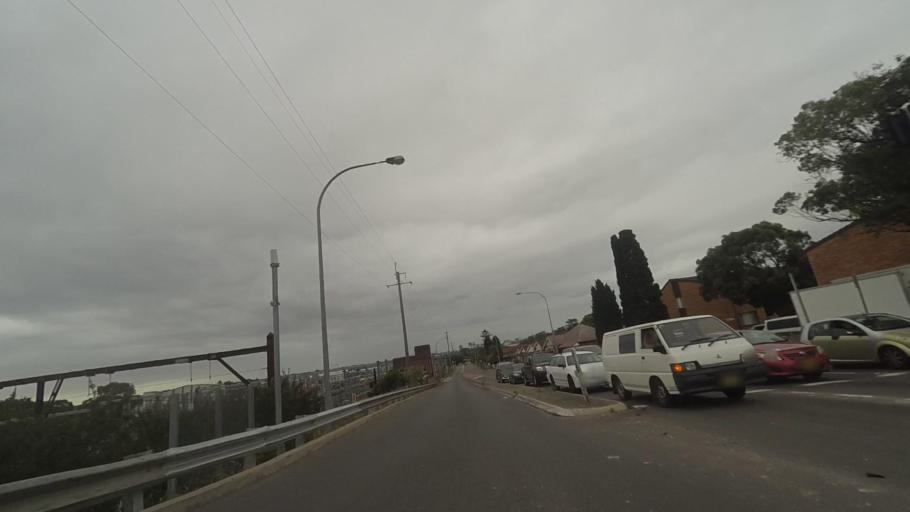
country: AU
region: New South Wales
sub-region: Auburn
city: Auburn
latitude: -33.8470
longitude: 151.0308
